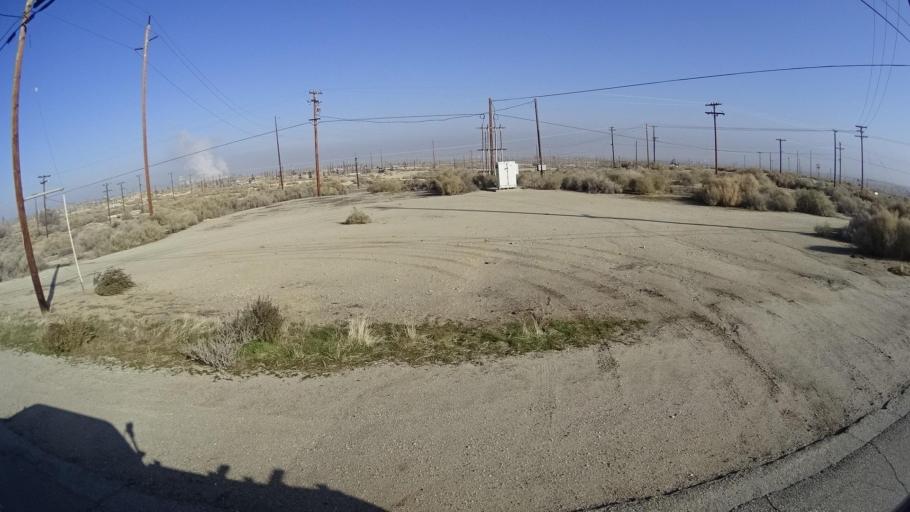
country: US
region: California
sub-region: Kern County
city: Taft Heights
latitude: 35.1939
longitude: -119.5814
